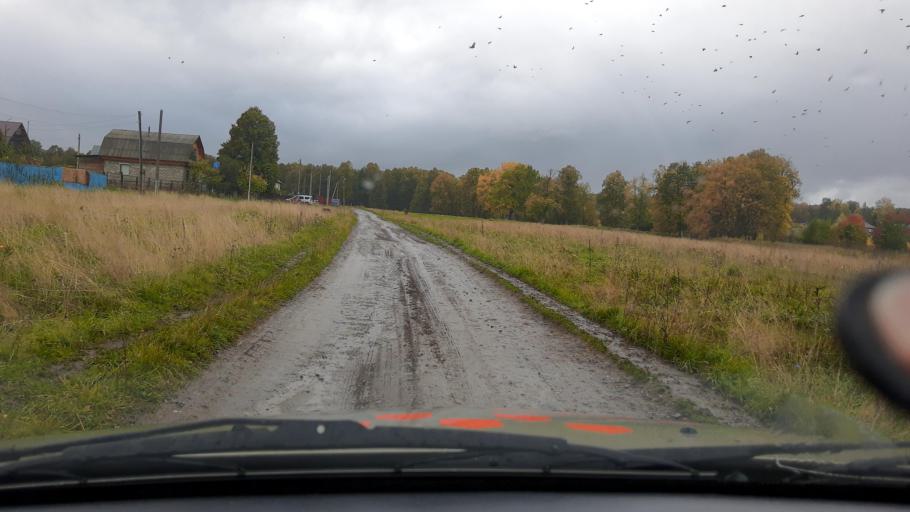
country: RU
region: Bashkortostan
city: Kudeyevskiy
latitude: 54.8760
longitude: 56.6284
